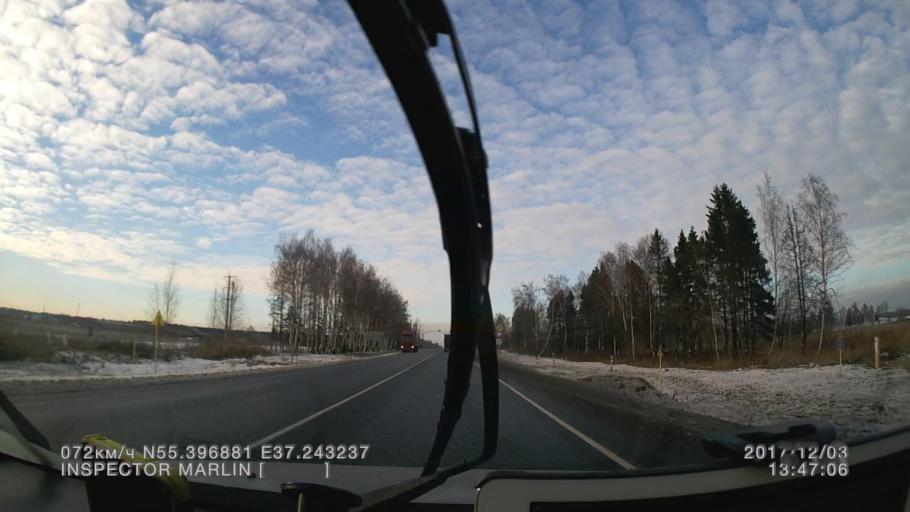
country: RU
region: Moskovskaya
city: Troitsk
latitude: 55.3968
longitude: 37.2435
